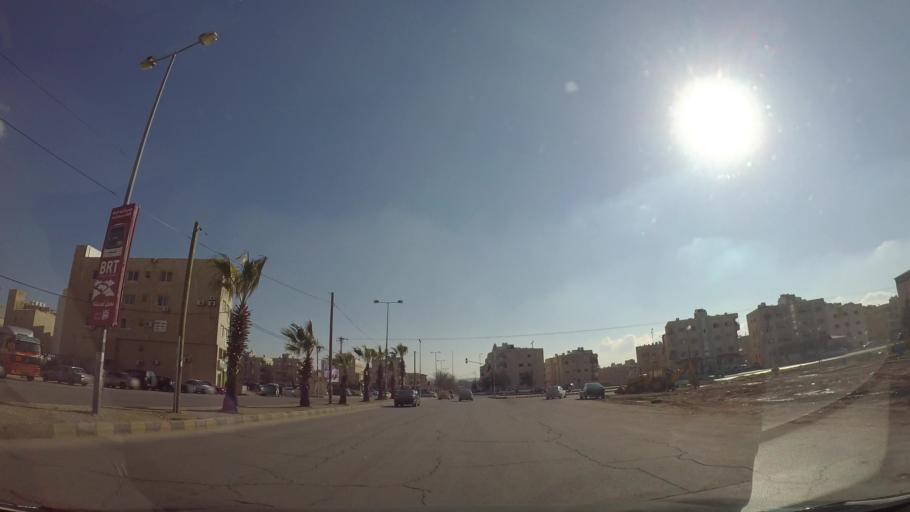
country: JO
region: Amman
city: Amman
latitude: 31.9811
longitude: 35.9404
